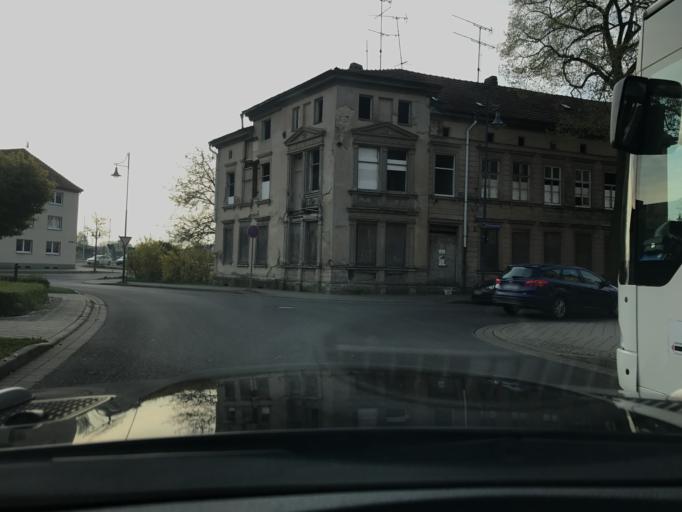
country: DE
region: Thuringia
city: Muehlhausen
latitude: 51.2085
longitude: 10.4730
